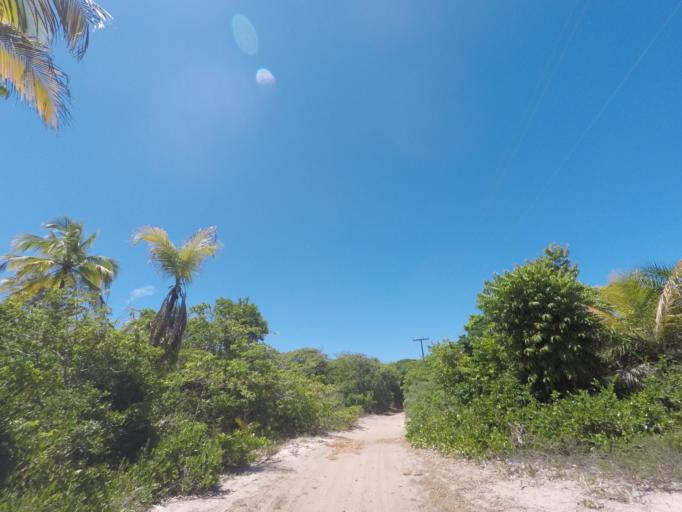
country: BR
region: Bahia
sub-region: Marau
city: Marau
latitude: -14.0092
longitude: -38.9447
